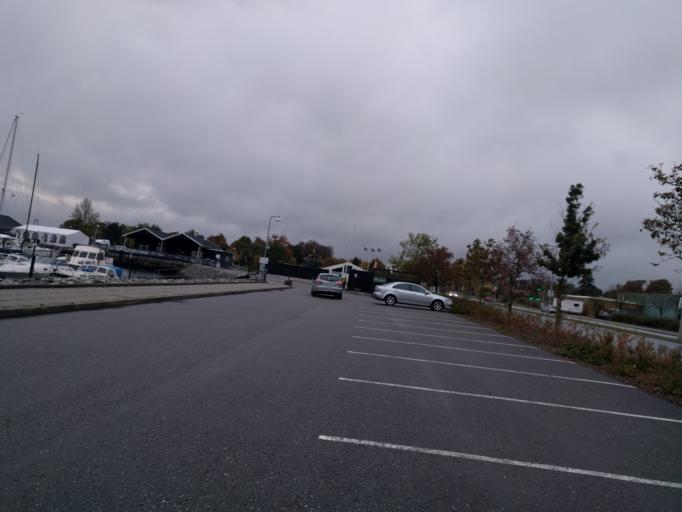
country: DK
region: South Denmark
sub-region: Fredericia Kommune
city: Fredericia
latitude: 55.5536
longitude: 9.7272
